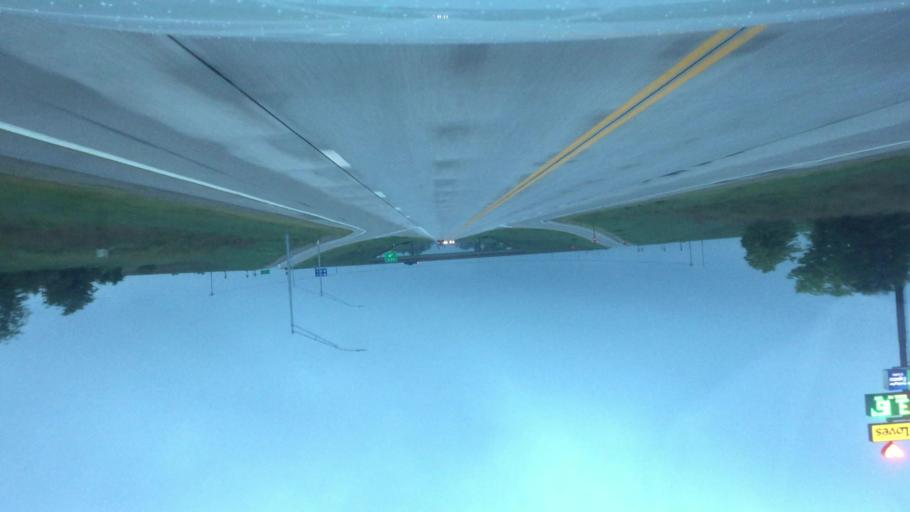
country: US
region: Kansas
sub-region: Neosho County
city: Chanute
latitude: 37.6489
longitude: -95.4797
